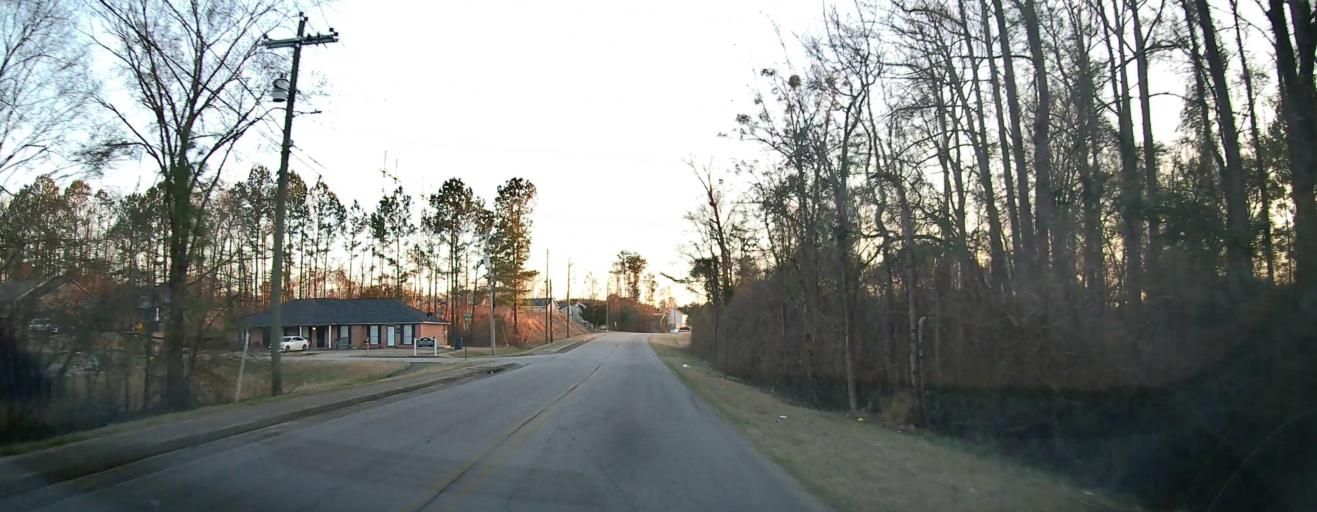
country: US
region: Georgia
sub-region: Troup County
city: La Grange
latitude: 33.0293
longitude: -85.0041
